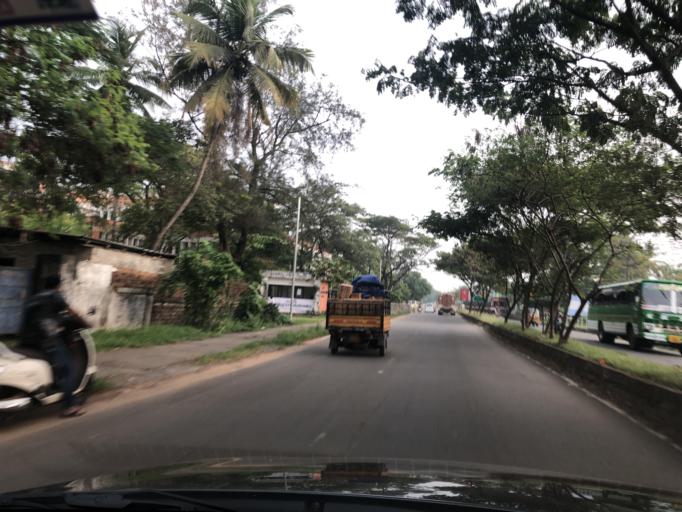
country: IN
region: Kerala
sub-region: Kozhikode
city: Kozhikode
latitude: 11.2852
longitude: 75.7605
